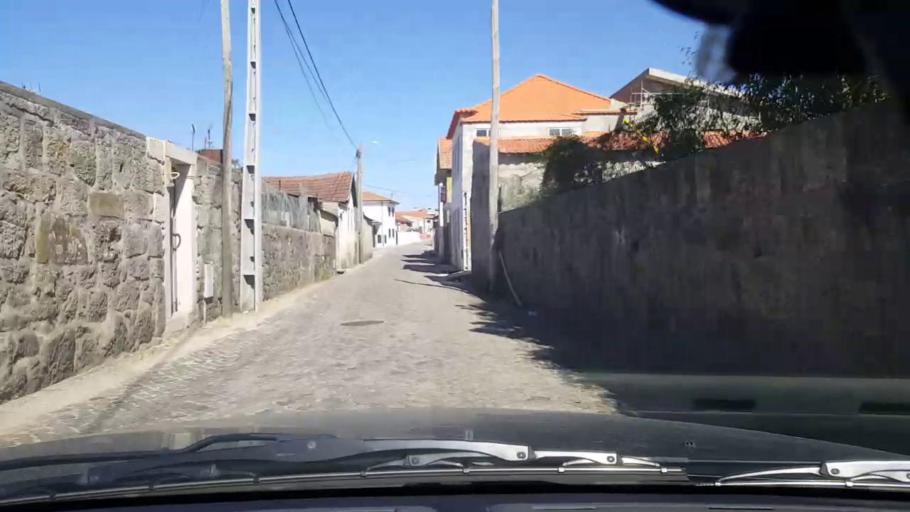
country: PT
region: Porto
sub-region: Maia
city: Gemunde
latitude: 41.2858
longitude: -8.6736
